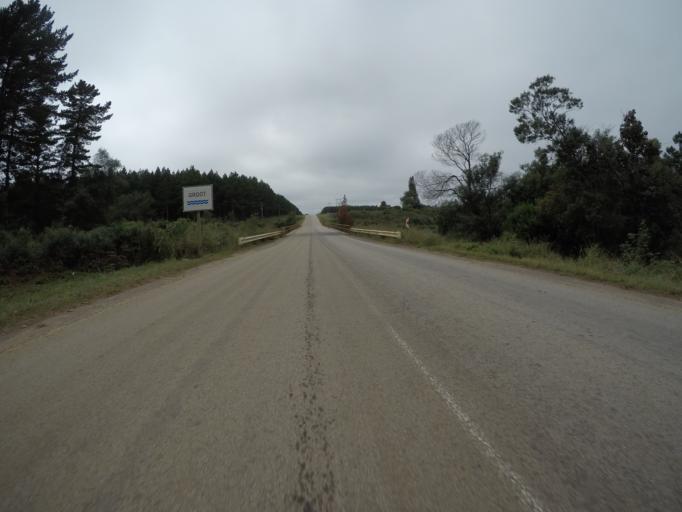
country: ZA
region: Eastern Cape
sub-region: Cacadu District Municipality
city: Kareedouw
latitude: -33.9948
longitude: 24.1226
